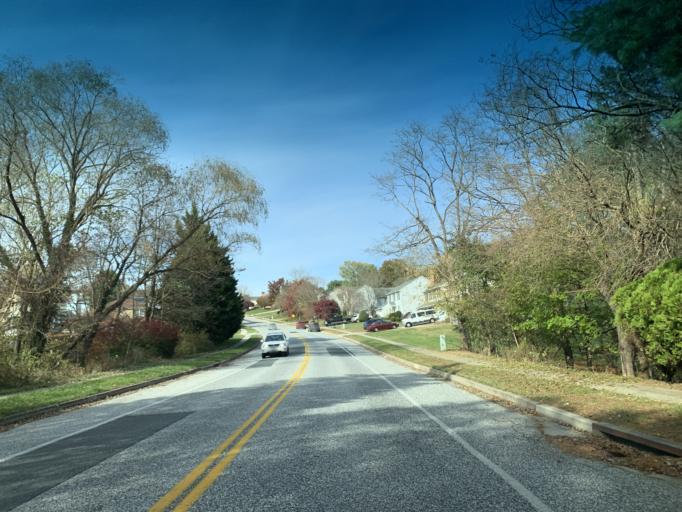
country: US
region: Maryland
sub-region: Harford County
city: South Bel Air
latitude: 39.5288
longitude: -76.3209
